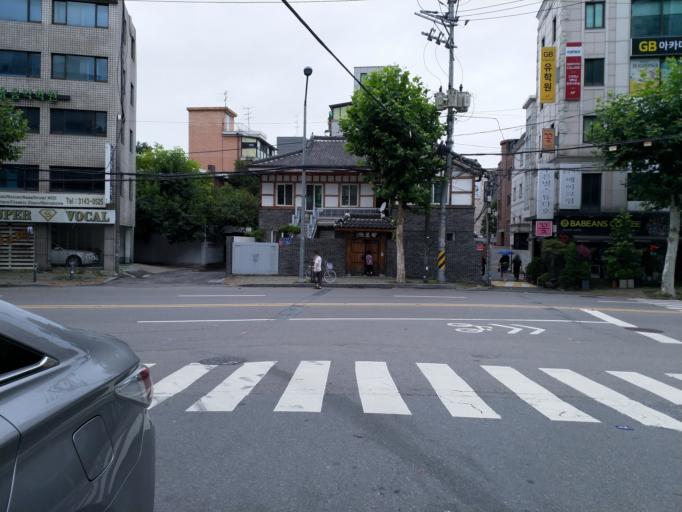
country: KR
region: Seoul
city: Seoul
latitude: 37.5568
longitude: 126.9222
